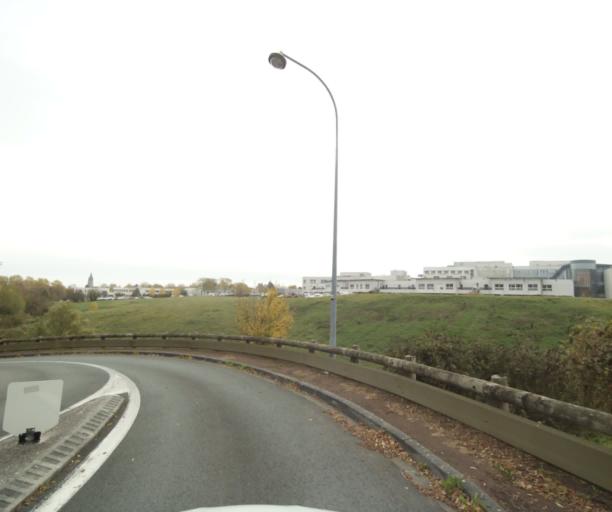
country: FR
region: Poitou-Charentes
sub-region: Departement de la Charente-Maritime
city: Saintes
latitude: 45.7484
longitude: -0.6551
